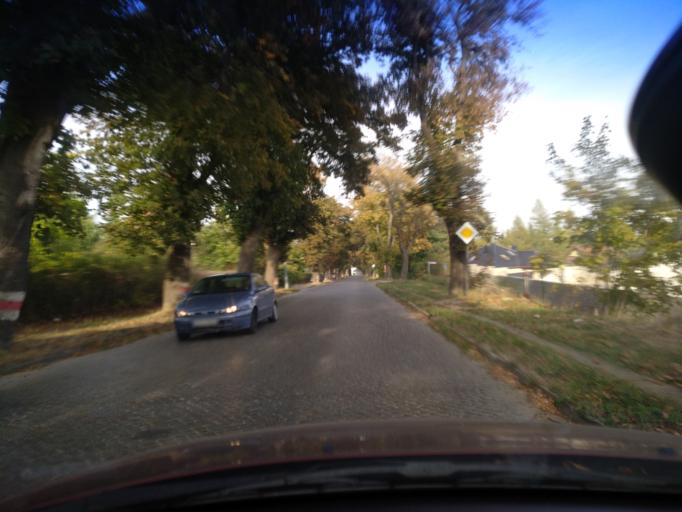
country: PL
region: Lower Silesian Voivodeship
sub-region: Powiat zgorzelecki
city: Zgorzelec
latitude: 51.1623
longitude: 15.0020
